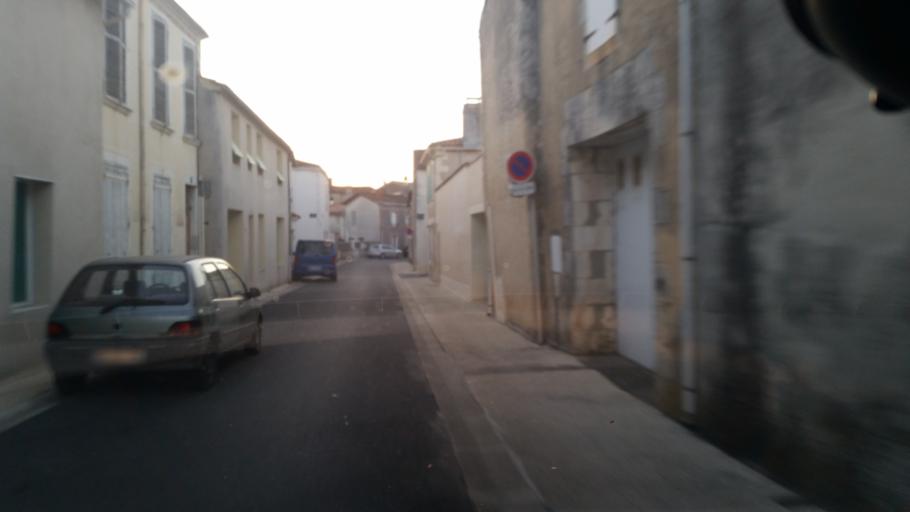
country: FR
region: Poitou-Charentes
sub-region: Departement de la Charente-Maritime
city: Marans
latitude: 46.3103
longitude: -0.9946
